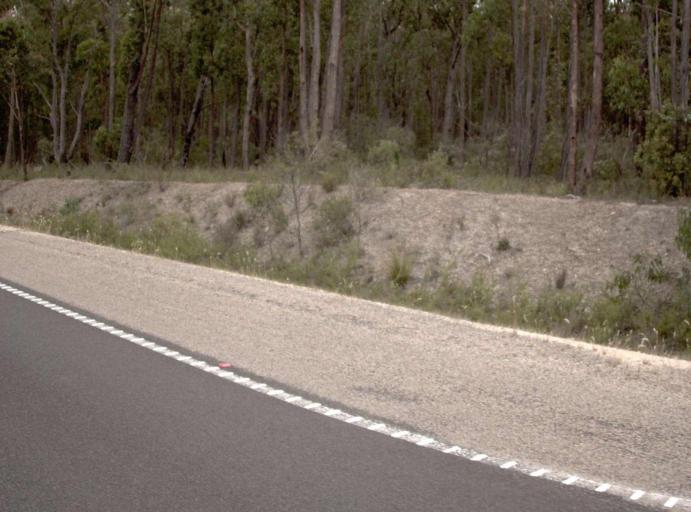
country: AU
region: Victoria
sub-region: East Gippsland
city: Lakes Entrance
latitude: -37.7044
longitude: 147.9927
